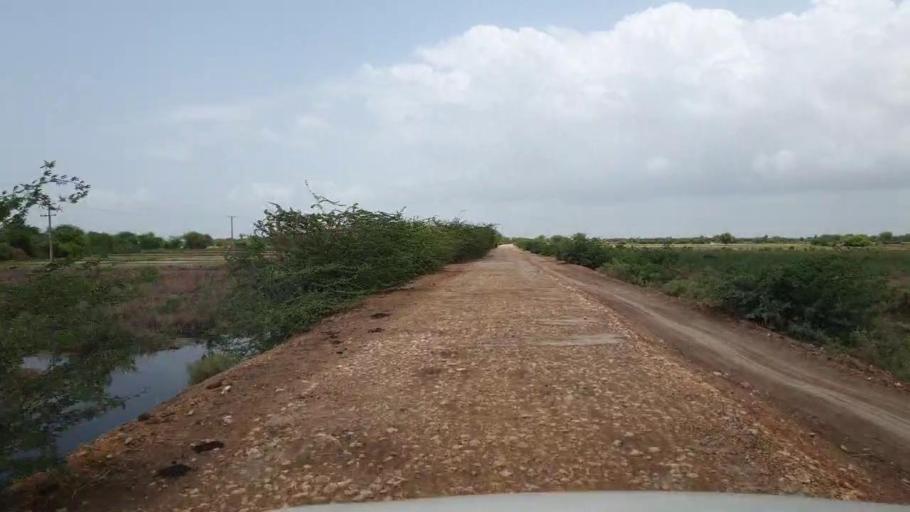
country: PK
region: Sindh
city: Kario
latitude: 24.6925
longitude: 68.6554
